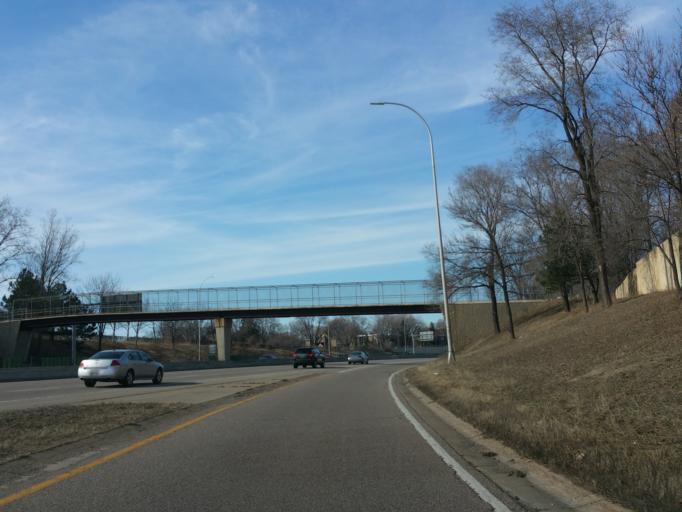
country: US
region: Minnesota
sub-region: Hennepin County
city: Bloomington
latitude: 44.8436
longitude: -93.2460
